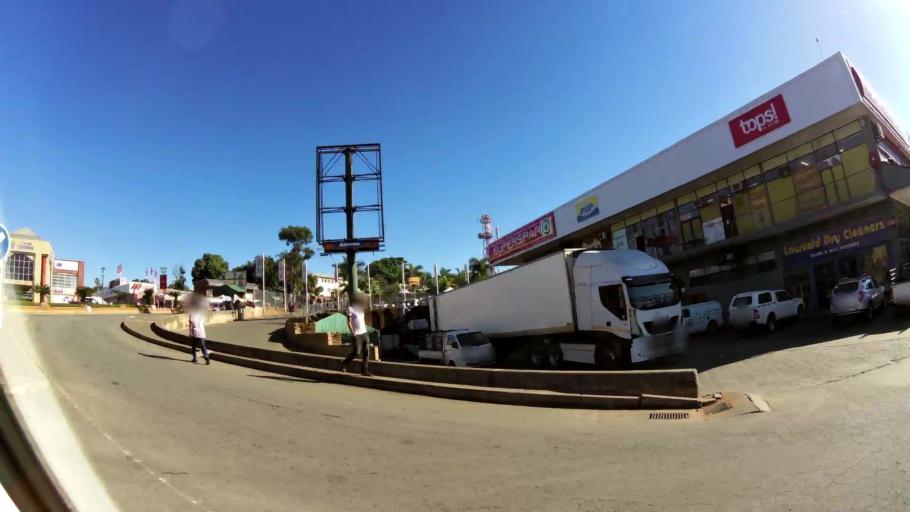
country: ZA
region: Limpopo
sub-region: Mopani District Municipality
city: Tzaneen
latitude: -23.8290
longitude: 30.1630
